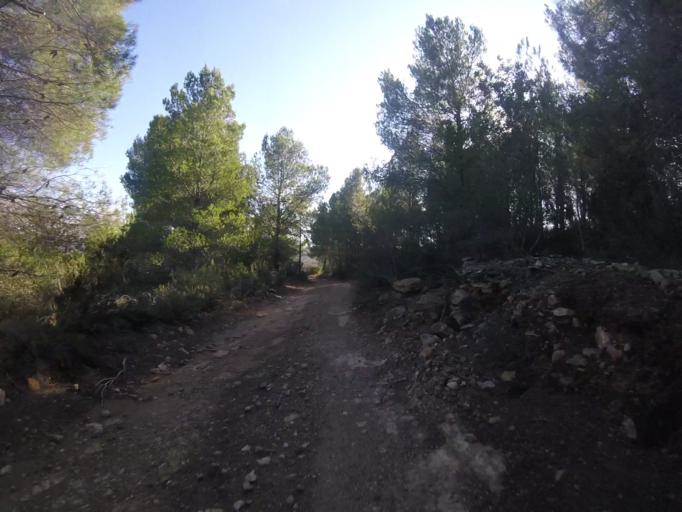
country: ES
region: Valencia
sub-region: Provincia de Castello
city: Sarratella
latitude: 40.2844
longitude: 0.0651
